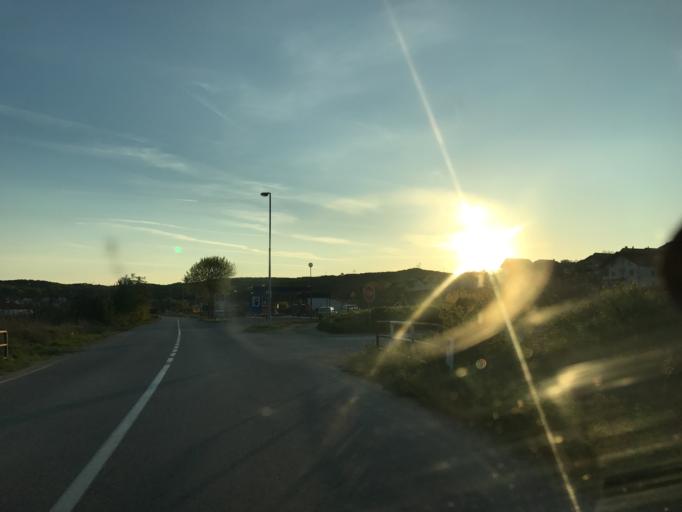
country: RO
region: Mehedinti
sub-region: Comuna Burila Mare
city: Burila Mare
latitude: 44.4875
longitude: 22.4617
